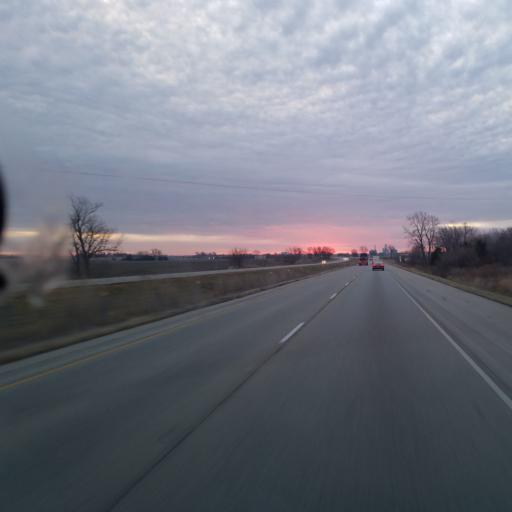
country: US
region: Illinois
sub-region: McLean County
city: Twin Grove
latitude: 40.5446
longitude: -89.0847
